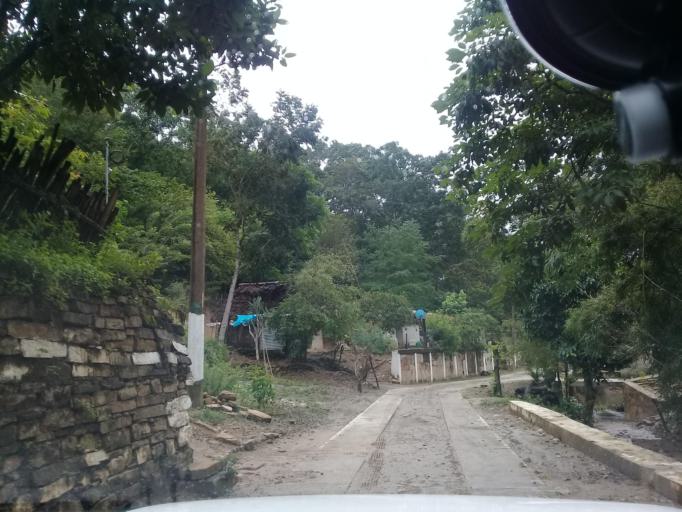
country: MX
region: Veracruz
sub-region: Chalma
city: San Pedro Coyutla
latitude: 21.2442
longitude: -98.4248
